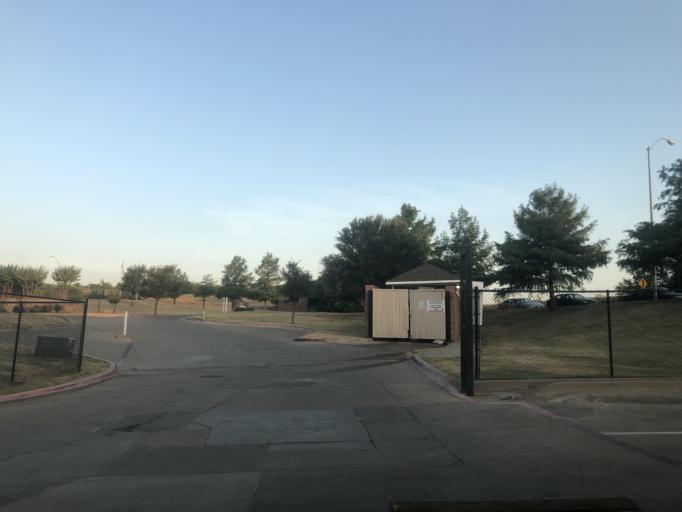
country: US
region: Texas
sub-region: Tarrant County
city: Sansom Park
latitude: 32.8050
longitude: -97.4182
